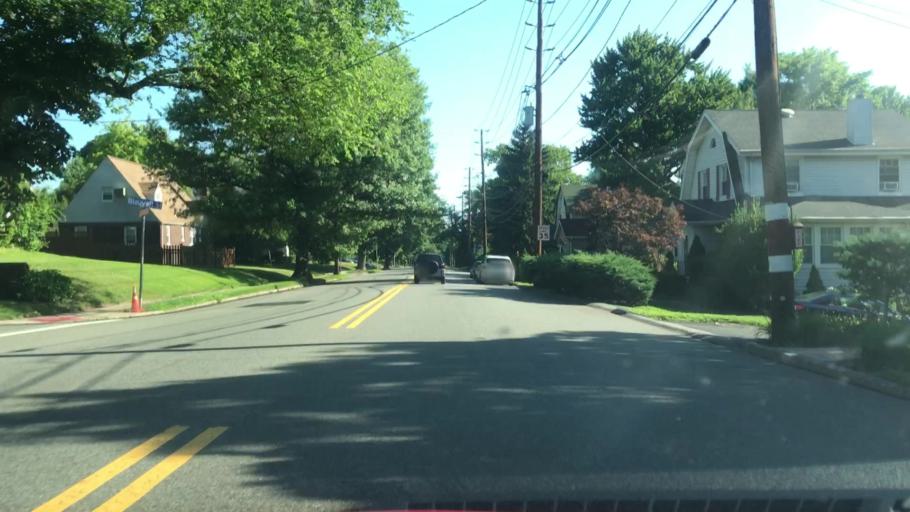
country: US
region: New Jersey
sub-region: Bergen County
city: Ridgefield Park
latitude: 40.8664
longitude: -74.0152
